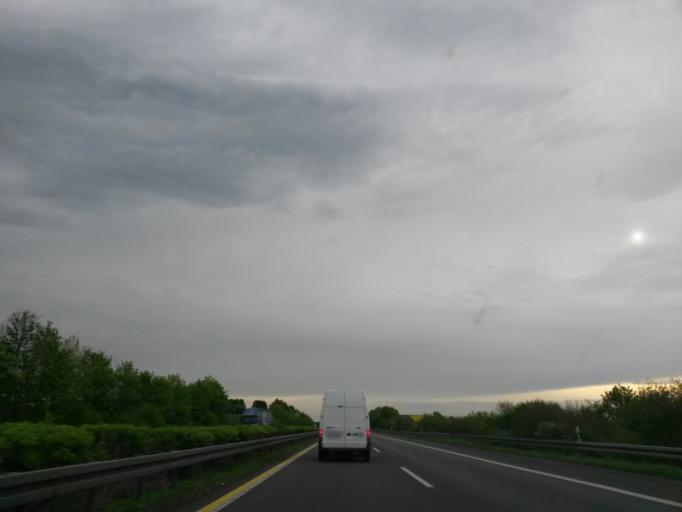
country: DE
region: Baden-Wuerttemberg
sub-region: Regierungsbezirk Stuttgart
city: Grossrinderfeld
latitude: 49.6597
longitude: 9.7539
